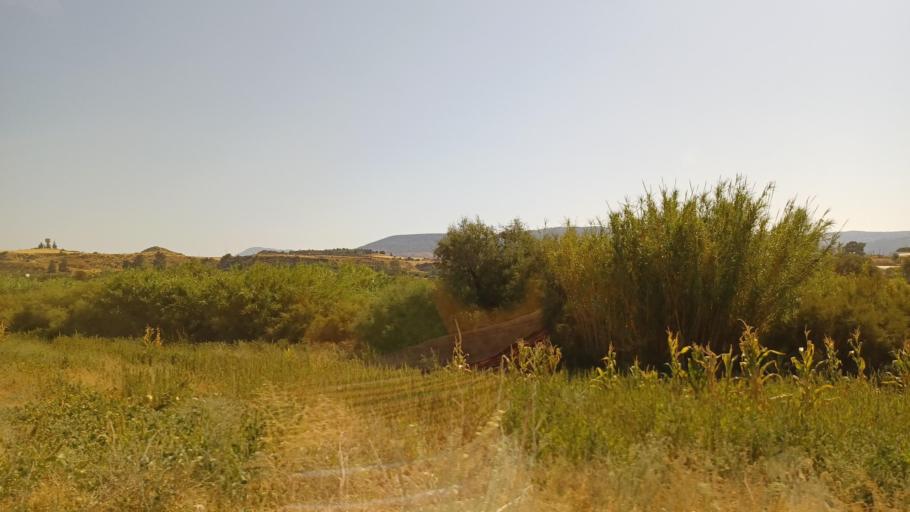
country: CY
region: Pafos
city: Polis
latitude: 35.0063
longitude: 32.4313
